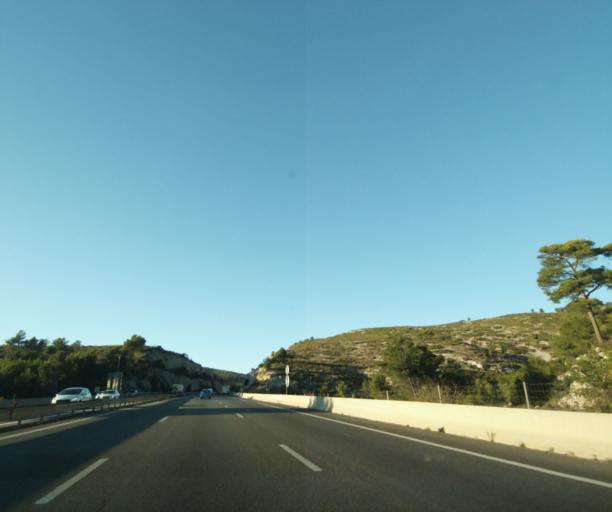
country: FR
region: Provence-Alpes-Cote d'Azur
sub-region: Departement des Bouches-du-Rhone
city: Cassis
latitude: 43.2093
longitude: 5.5846
